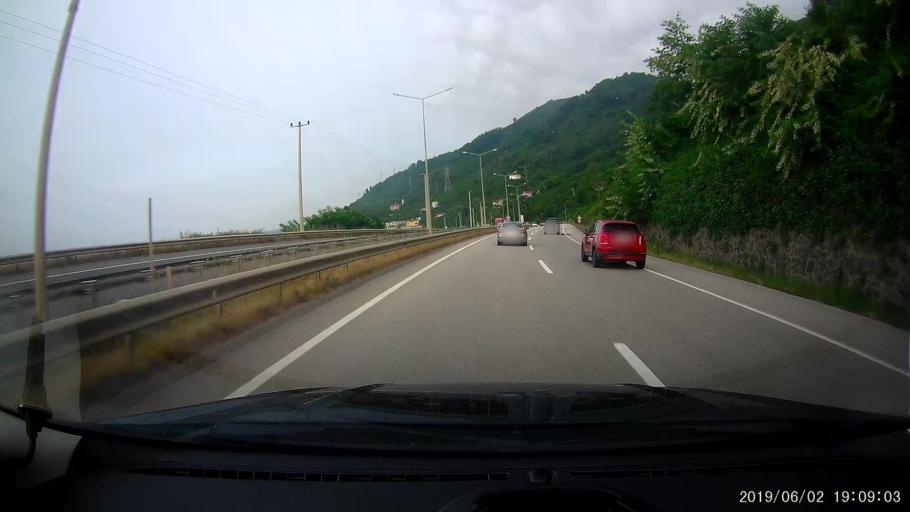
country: TR
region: Ordu
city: Gulyali
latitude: 40.9754
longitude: 38.0212
